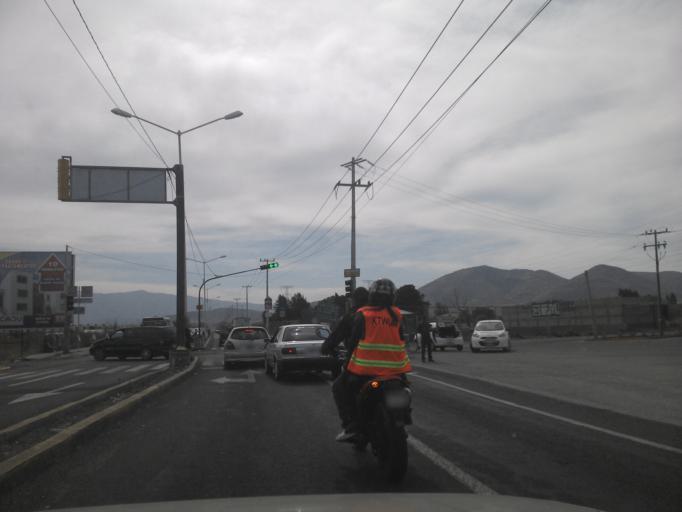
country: MX
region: Jalisco
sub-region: Tlajomulco de Zuniga
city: Hacienda los Fresnos
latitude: 20.5383
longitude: -103.4042
